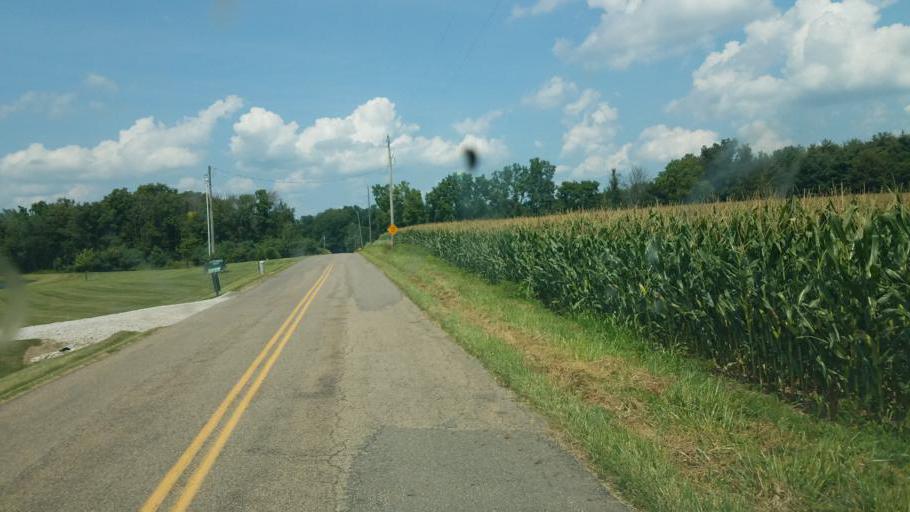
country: US
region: Ohio
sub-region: Knox County
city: Fredericktown
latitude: 40.4104
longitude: -82.5972
